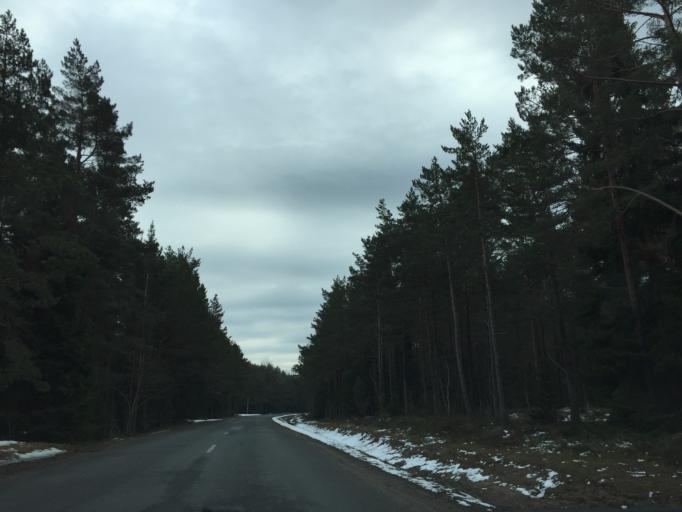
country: EE
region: Saare
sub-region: Kuressaare linn
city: Kuressaare
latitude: 58.4277
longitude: 22.0725
